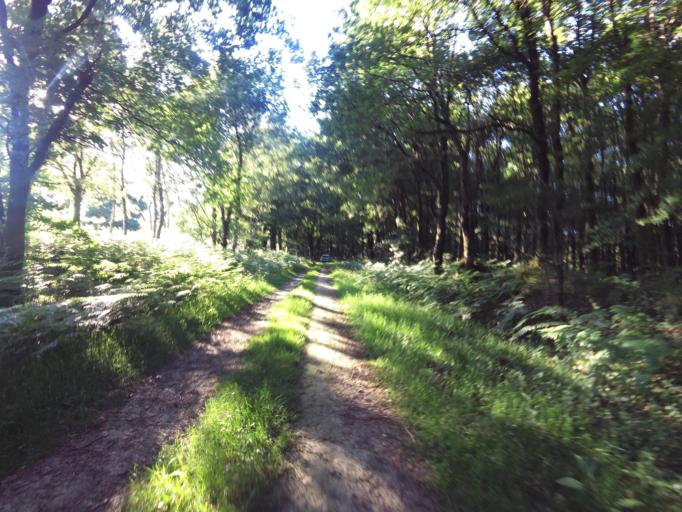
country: FR
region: Brittany
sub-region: Departement du Morbihan
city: Molac
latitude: 47.7452
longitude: -2.4344
